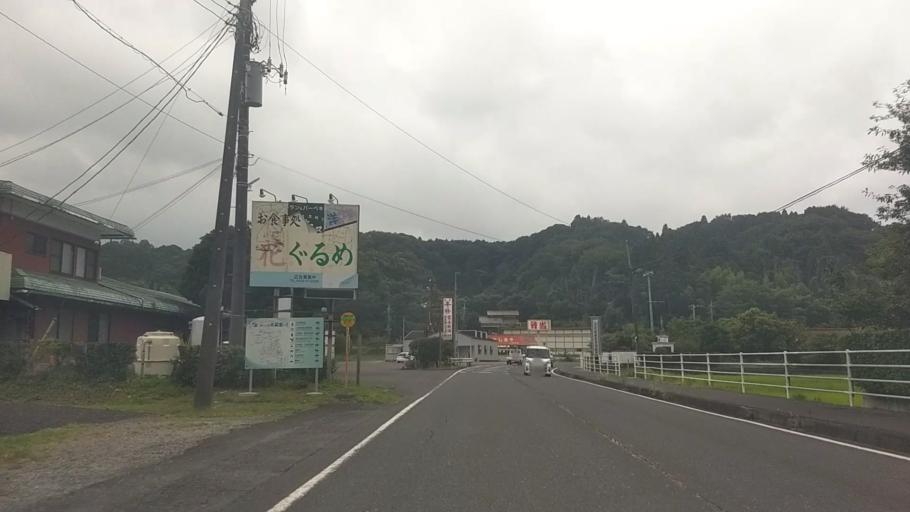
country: JP
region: Chiba
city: Kisarazu
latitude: 35.2872
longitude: 140.0832
